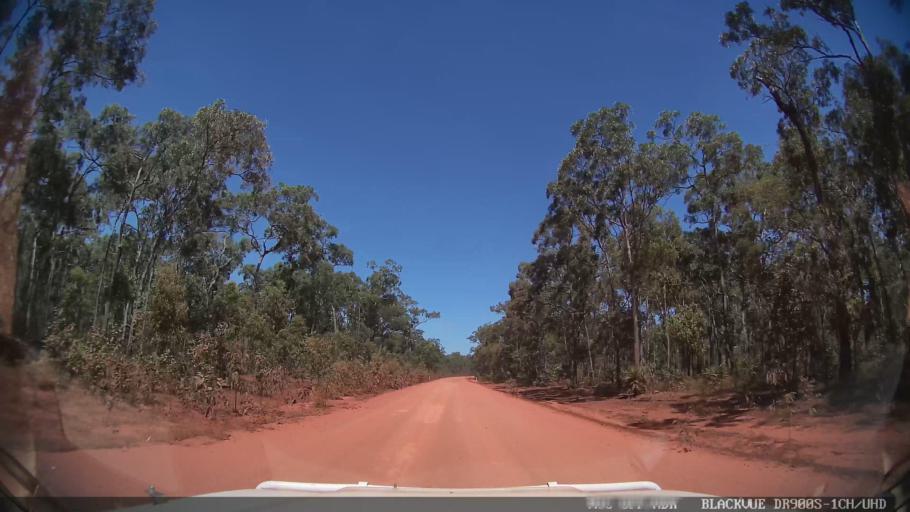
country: AU
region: Queensland
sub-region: Torres
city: Thursday Island
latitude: -11.1756
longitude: 142.2523
